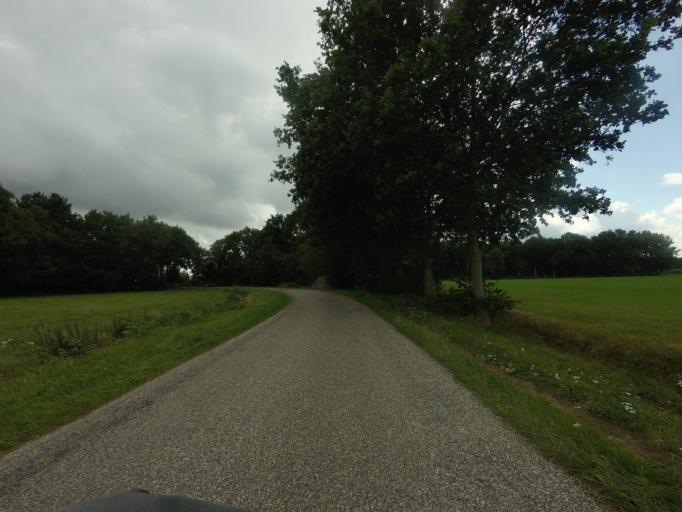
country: NL
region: Friesland
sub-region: Gemeente Heerenveen
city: Jubbega
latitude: 52.9836
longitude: 6.2763
